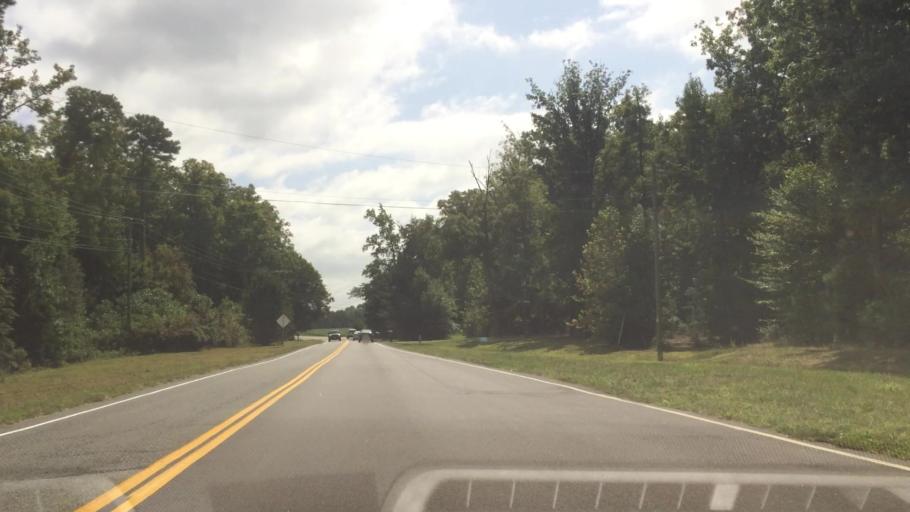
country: US
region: Virginia
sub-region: Henrico County
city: Chamberlayne
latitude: 37.6888
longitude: -77.4376
